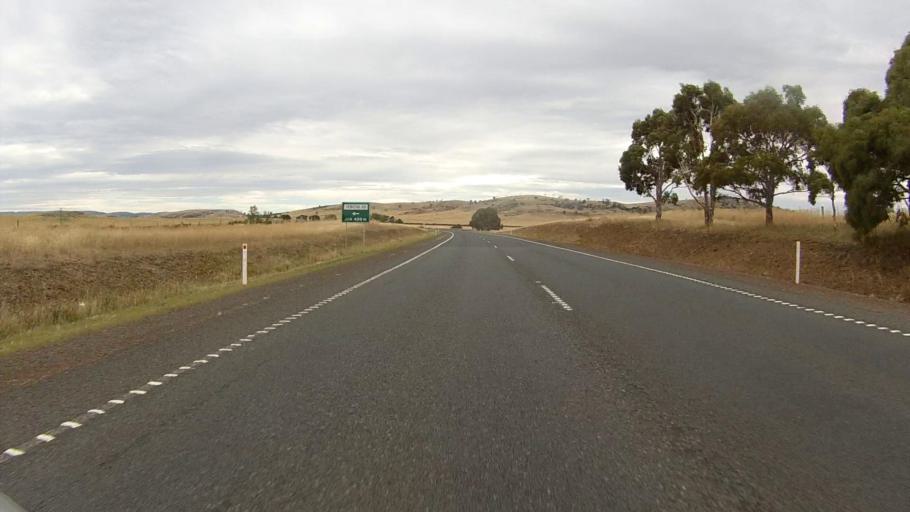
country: AU
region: Tasmania
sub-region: Brighton
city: Bridgewater
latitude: -42.3731
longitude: 147.3307
